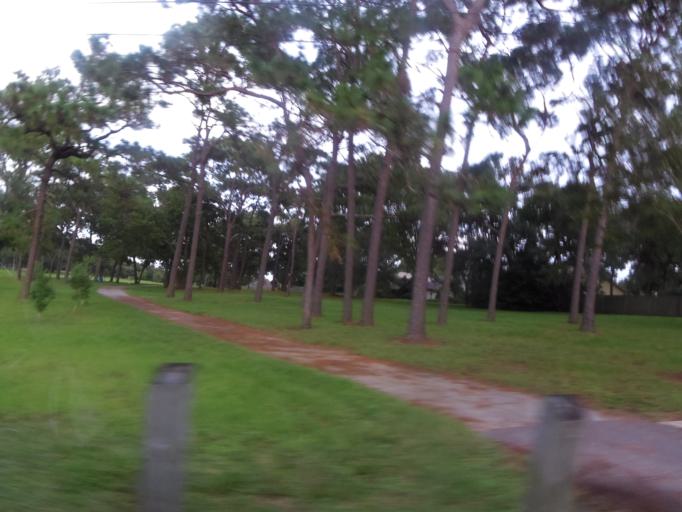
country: US
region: Florida
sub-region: Duval County
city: Atlantic Beach
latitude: 30.3622
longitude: -81.5070
